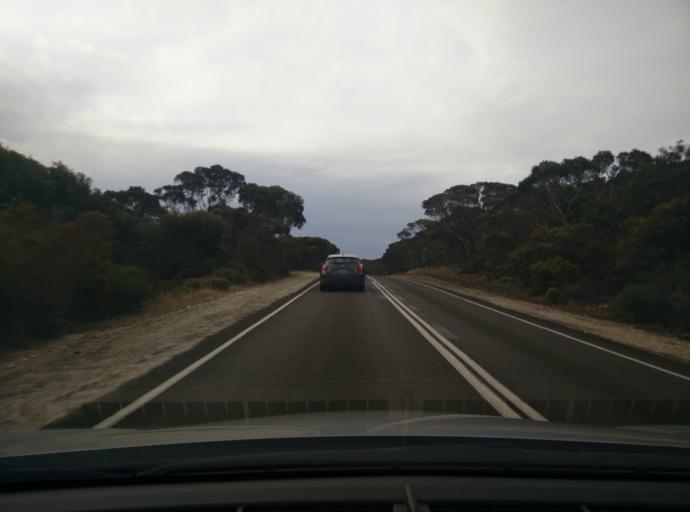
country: AU
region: South Australia
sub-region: Kangaroo Island
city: Kingscote
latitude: -35.7697
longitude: 137.6220
